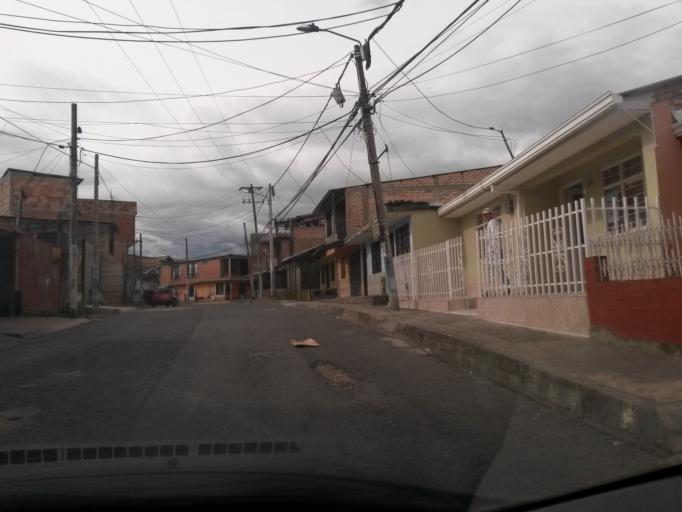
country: CO
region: Cauca
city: Popayan
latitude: 2.4506
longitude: -76.6259
